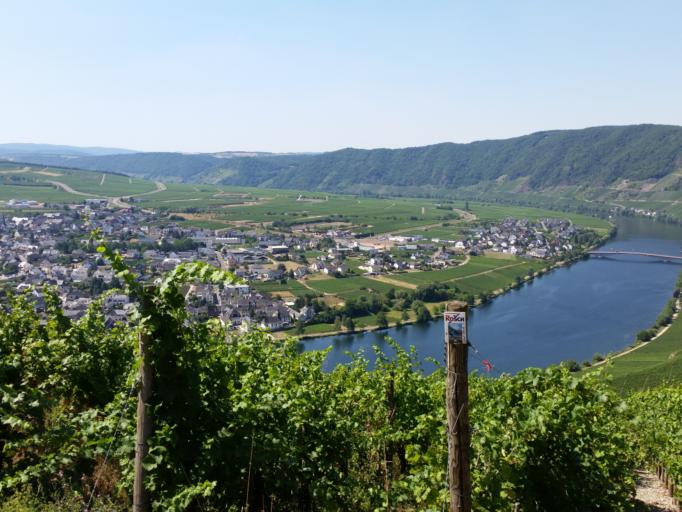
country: DE
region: Rheinland-Pfalz
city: Wintrich
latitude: 49.8879
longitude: 6.9346
